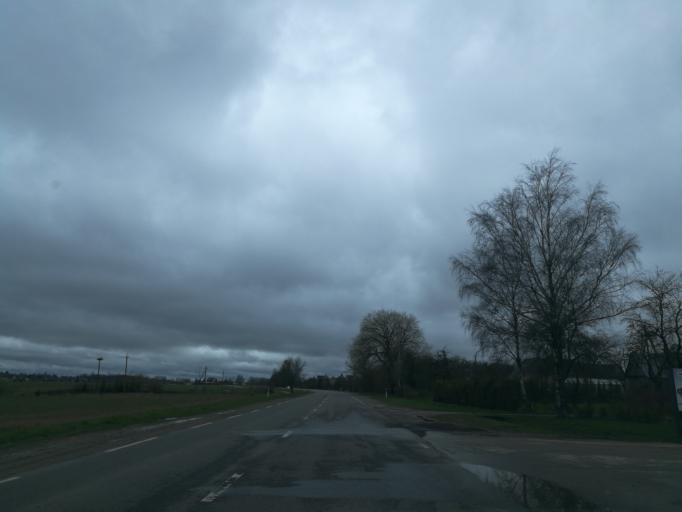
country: LT
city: Raseiniai
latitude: 55.4006
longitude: 23.1497
